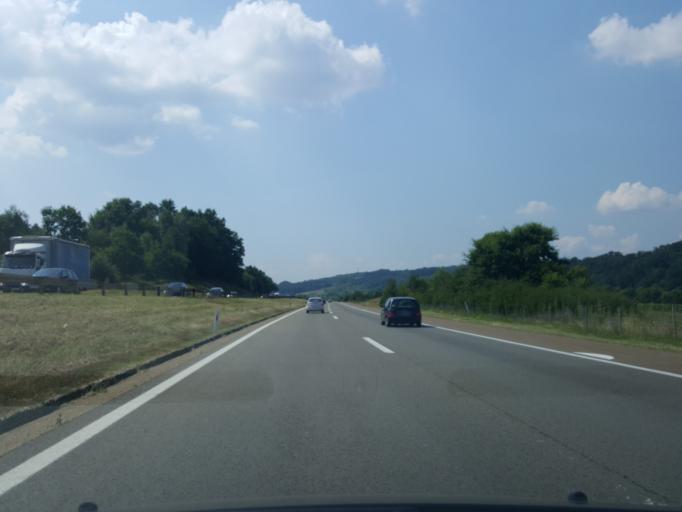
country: RS
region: Central Serbia
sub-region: Belgrade
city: Sopot
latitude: 44.5995
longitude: 20.6402
